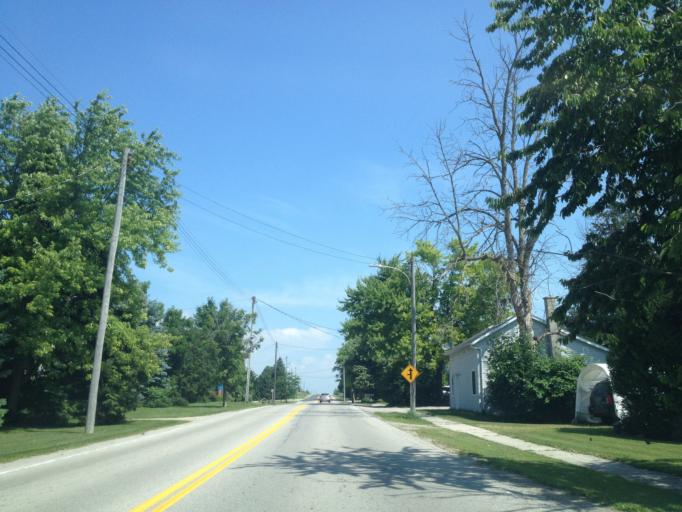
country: CA
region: Ontario
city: Huron East
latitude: 43.3904
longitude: -81.2220
